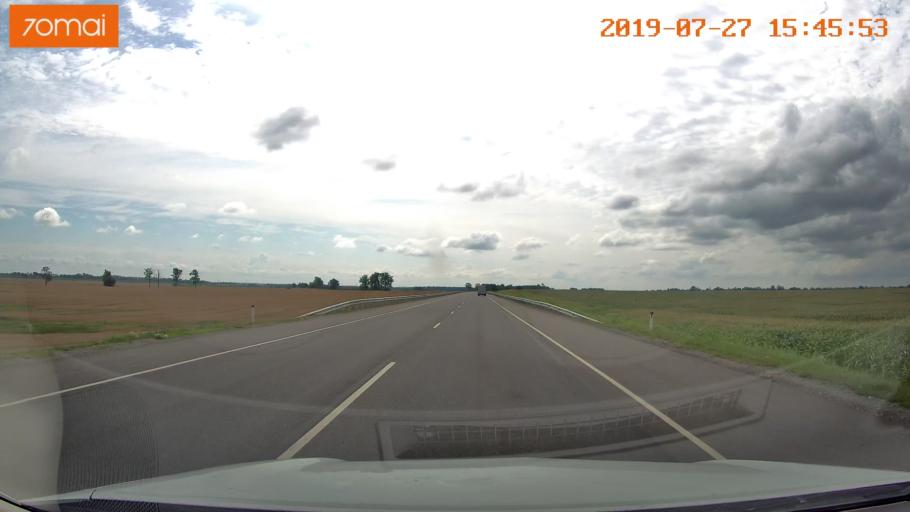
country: RU
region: Kaliningrad
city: Gusev
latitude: 54.6079
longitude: 22.1278
